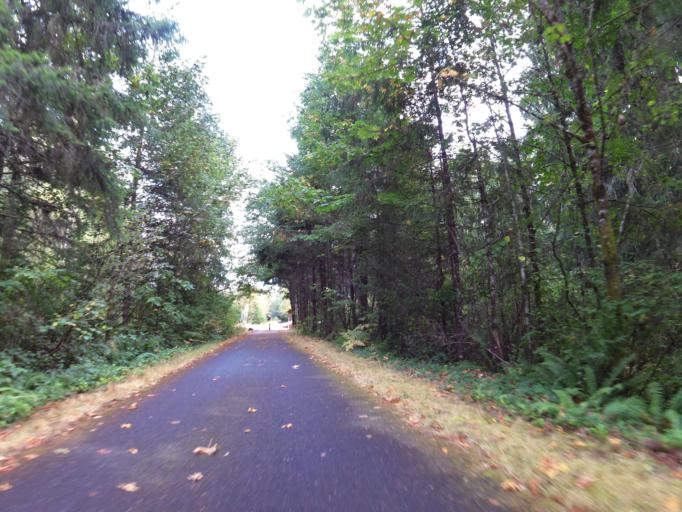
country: US
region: Washington
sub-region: Thurston County
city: Tenino
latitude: 46.9220
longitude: -122.8063
